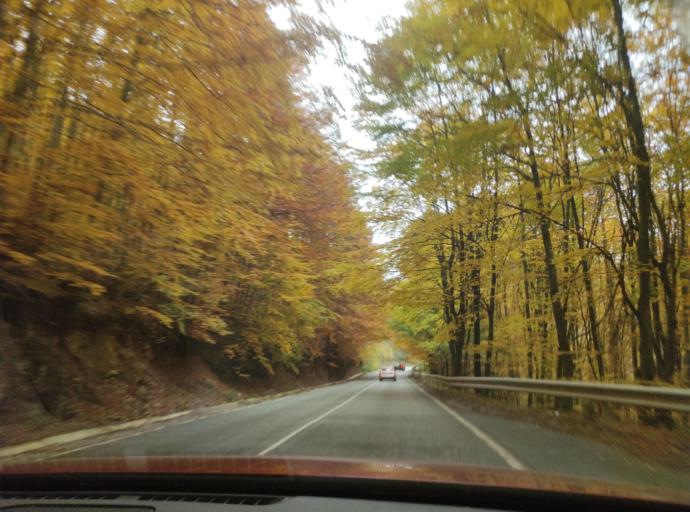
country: BG
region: Sofiya
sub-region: Obshtina Godech
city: Godech
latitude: 43.0254
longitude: 23.1370
